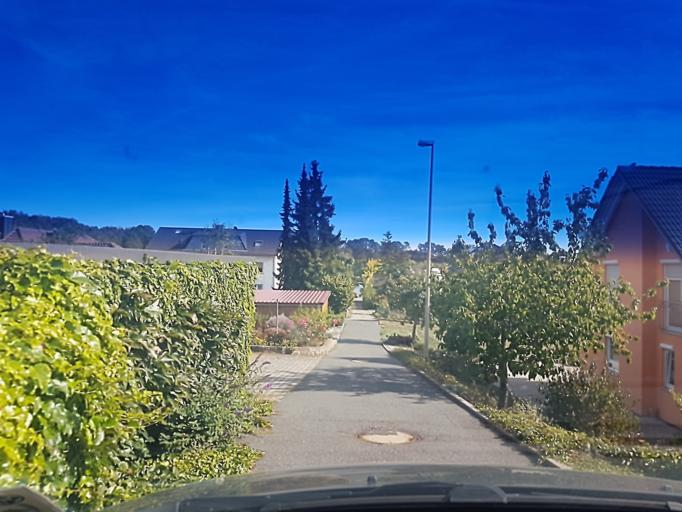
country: DE
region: Bavaria
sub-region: Upper Franconia
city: Schlusselfeld
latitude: 49.7619
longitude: 10.6208
